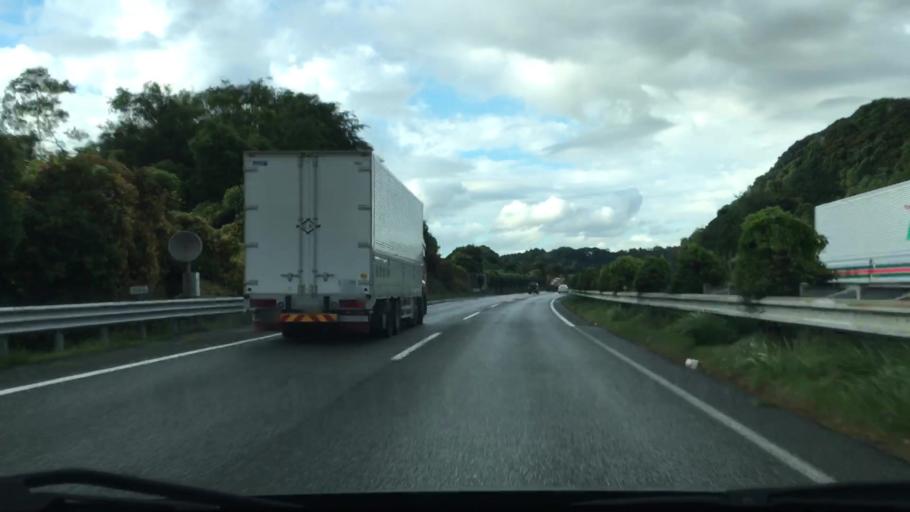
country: JP
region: Fukuoka
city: Koga
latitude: 33.7040
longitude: 130.4852
